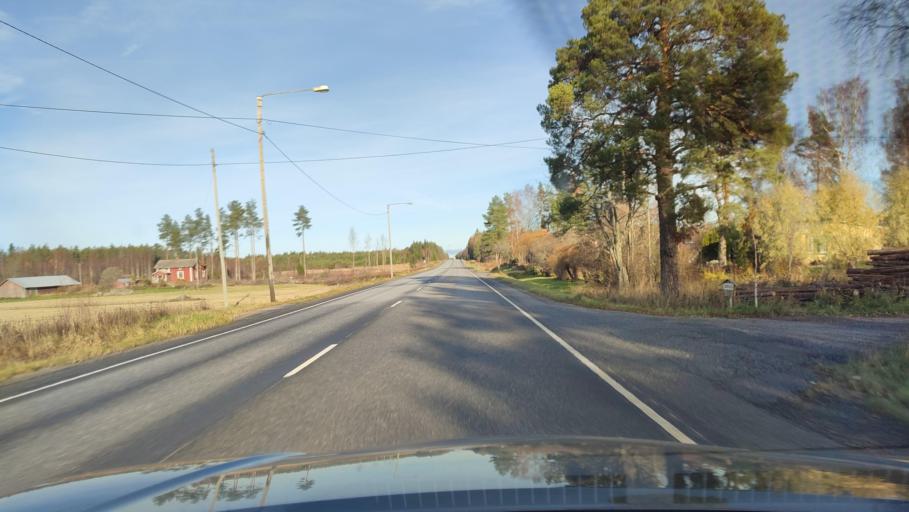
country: FI
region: Ostrobothnia
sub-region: Vaasa
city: Malax
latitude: 62.7811
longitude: 21.6644
